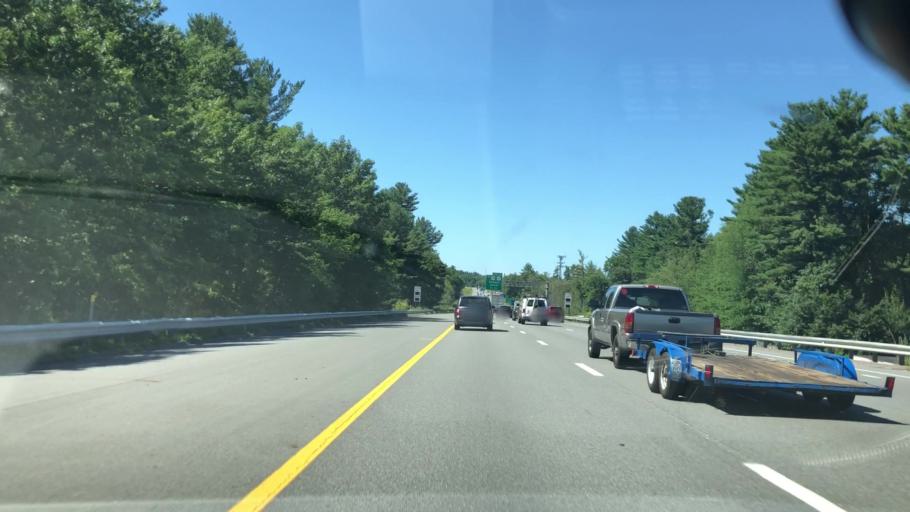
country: US
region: New Hampshire
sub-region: Rockingham County
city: Salem
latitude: 42.7662
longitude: -71.2370
